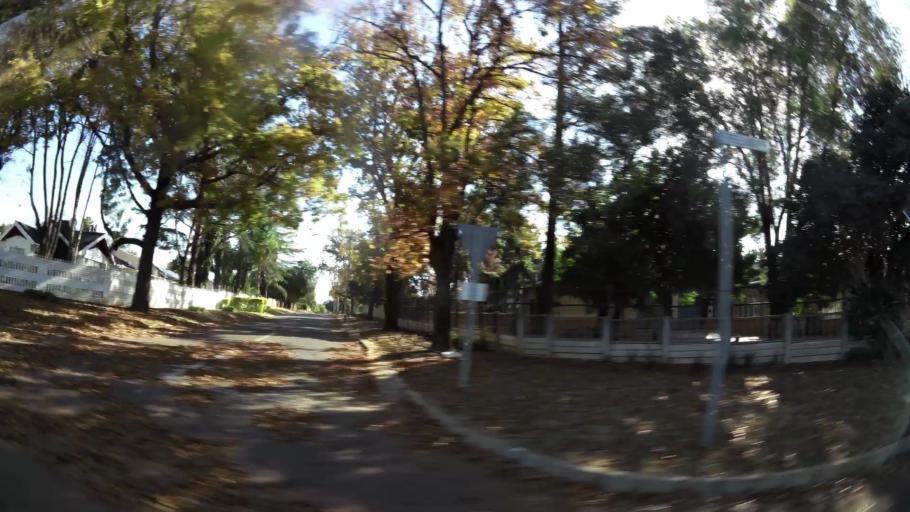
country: ZA
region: Gauteng
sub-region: City of Tshwane Metropolitan Municipality
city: Pretoria
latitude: -25.7265
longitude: 28.2616
